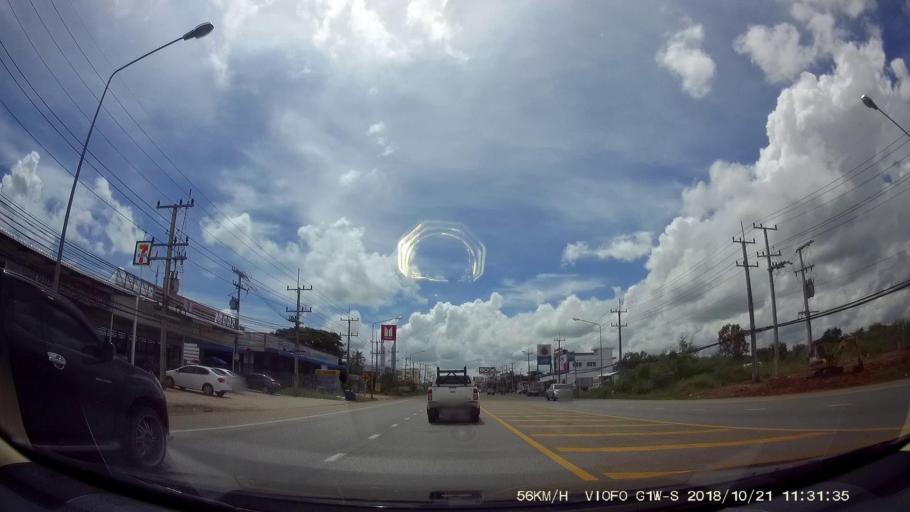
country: TH
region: Chaiyaphum
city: Chaiyaphum
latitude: 15.7680
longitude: 102.0255
